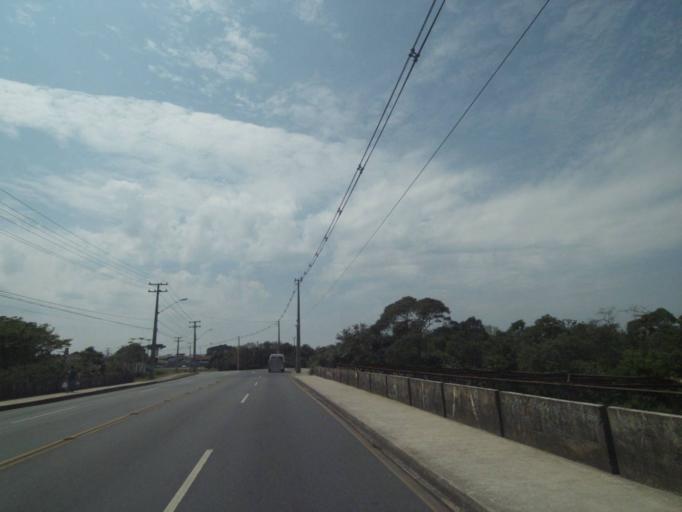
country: BR
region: Parana
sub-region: Curitiba
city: Curitiba
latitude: -25.4782
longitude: -49.3312
